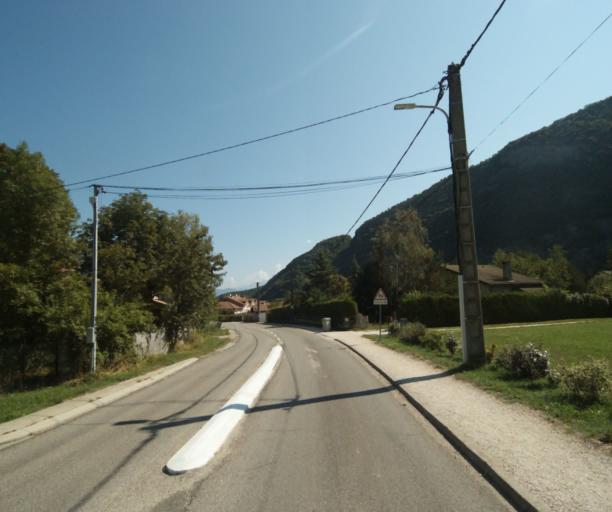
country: FR
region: Rhone-Alpes
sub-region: Departement de l'Isere
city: Saint-Paul-de-Varces
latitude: 45.0739
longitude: 5.6592
